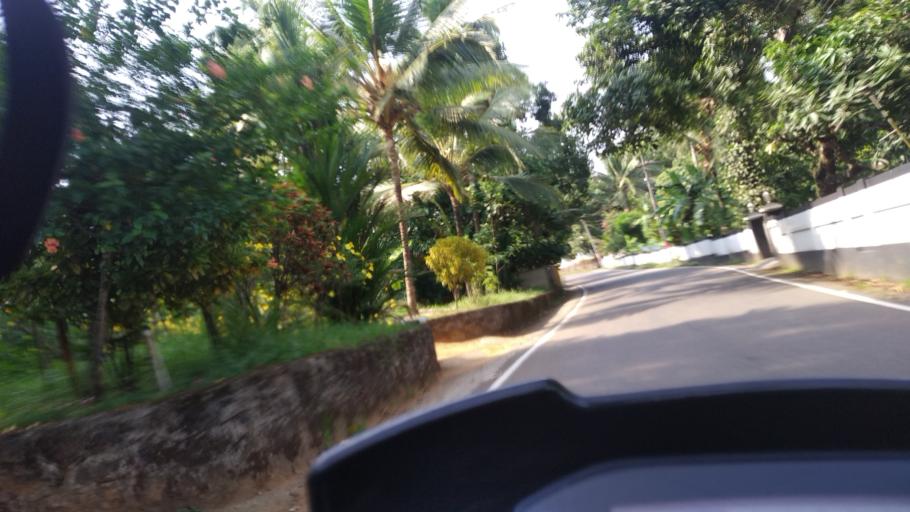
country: IN
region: Kerala
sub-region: Ernakulam
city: Piravam
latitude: 9.8377
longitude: 76.5380
